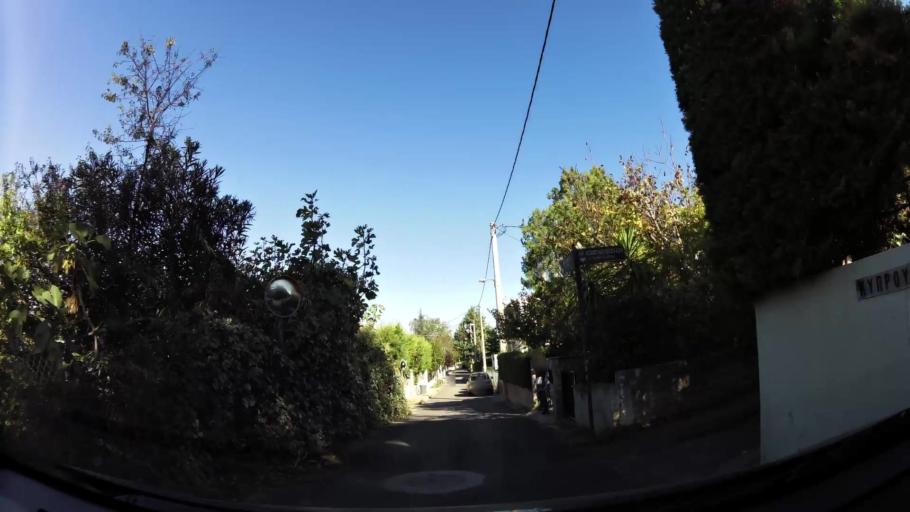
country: GR
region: Attica
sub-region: Nomarchia Anatolikis Attikis
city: Anoixi
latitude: 38.1341
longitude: 23.8629
